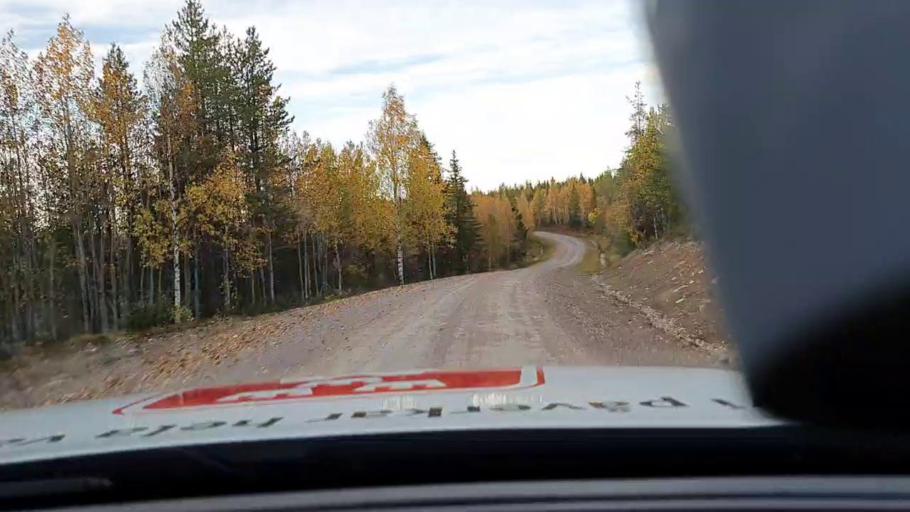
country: SE
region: Norrbotten
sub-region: Lulea Kommun
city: Ranea
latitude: 66.2668
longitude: 22.2592
